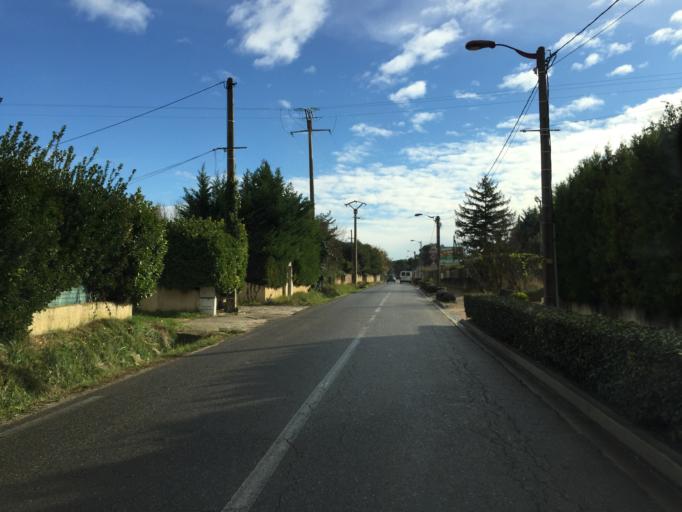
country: FR
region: Provence-Alpes-Cote d'Azur
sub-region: Departement du Vaucluse
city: Althen-des-Paluds
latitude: 44.0049
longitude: 4.9461
